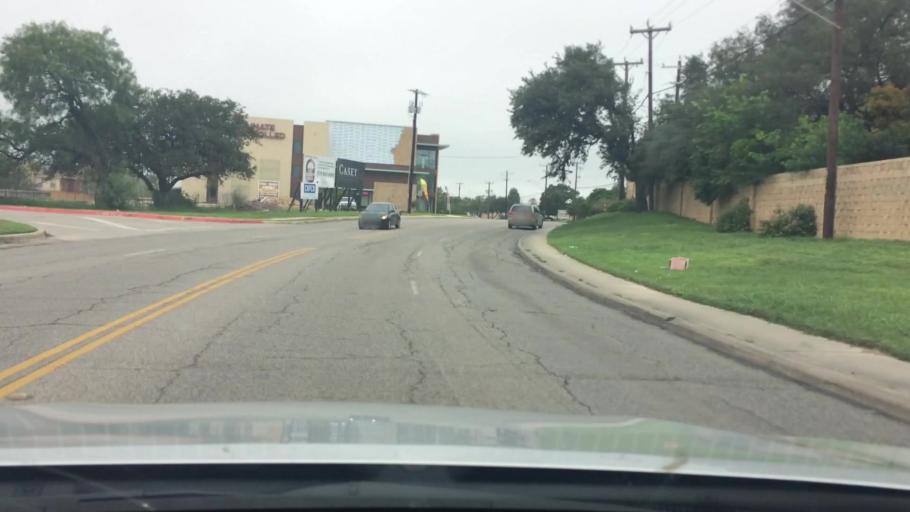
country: US
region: Texas
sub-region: Bexar County
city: Hollywood Park
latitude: 29.5831
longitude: -98.4480
